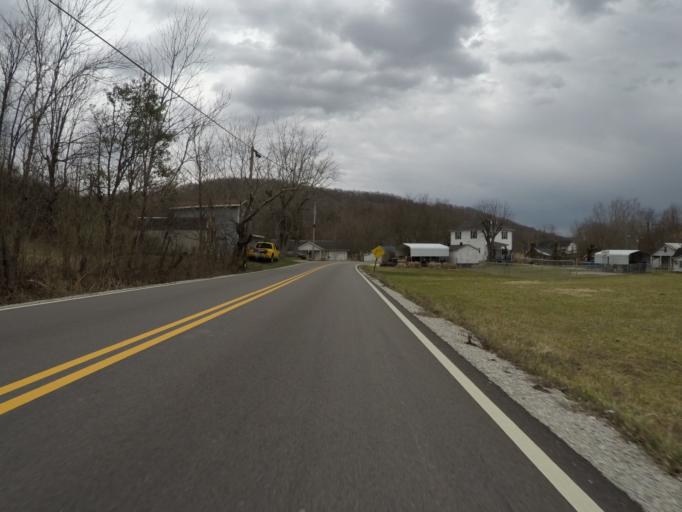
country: US
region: Ohio
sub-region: Lawrence County
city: Burlington
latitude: 38.4472
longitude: -82.5056
